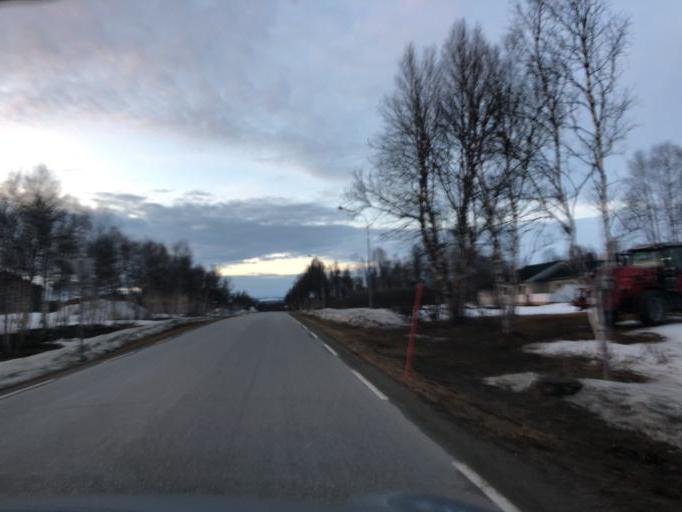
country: NO
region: Sor-Trondelag
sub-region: Tydal
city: Aas
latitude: 62.6473
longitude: 11.8653
